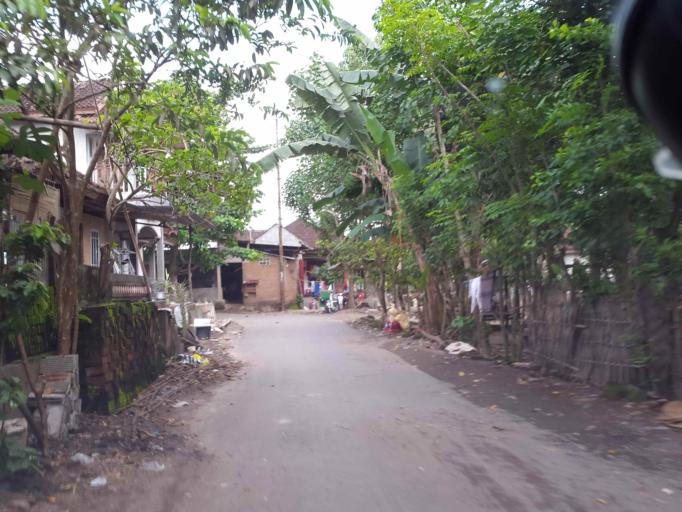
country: ID
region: West Nusa Tenggara
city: Mambalan
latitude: -8.5443
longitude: 116.1012
